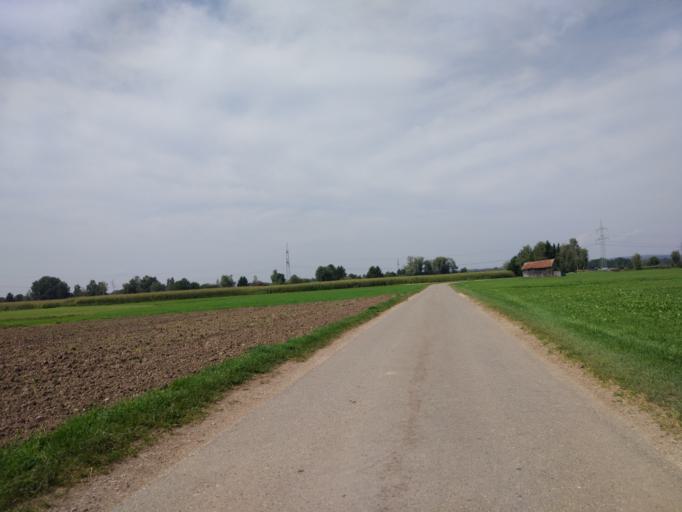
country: DE
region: Baden-Wuerttemberg
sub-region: Tuebingen Region
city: Achstetten
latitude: 48.2841
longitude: 9.8951
